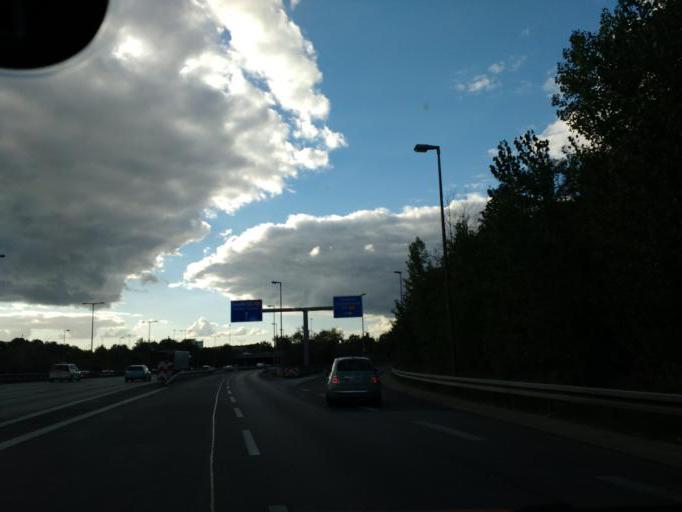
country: DE
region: Berlin
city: Schoneberg Bezirk
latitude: 52.4738
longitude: 13.3556
